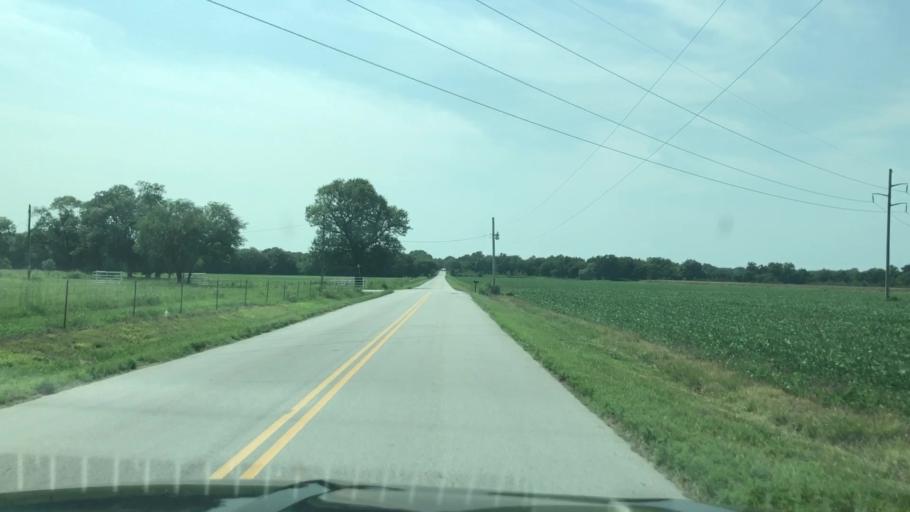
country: US
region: Oklahoma
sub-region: Ottawa County
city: Commerce
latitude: 36.9291
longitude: -94.8502
